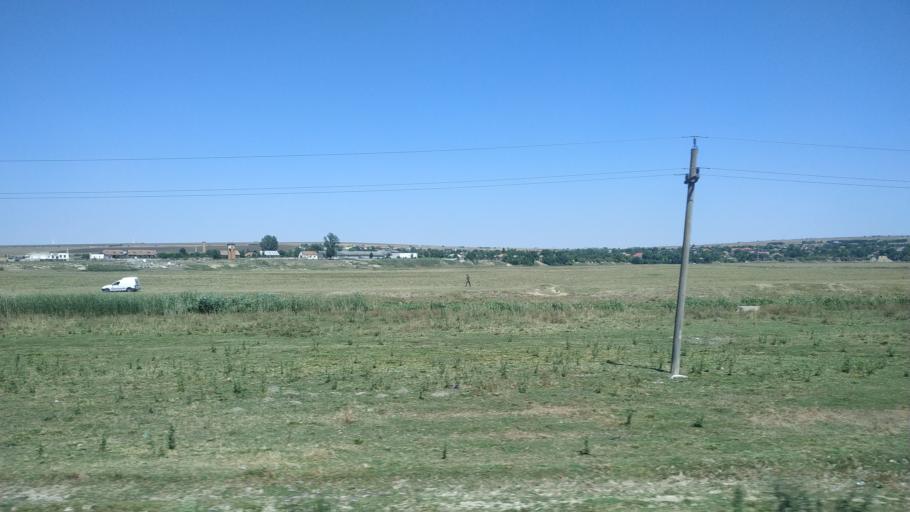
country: RO
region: Constanta
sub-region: Comuna Mircea Voda
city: Satu Nou
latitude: 44.2591
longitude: 28.2179
